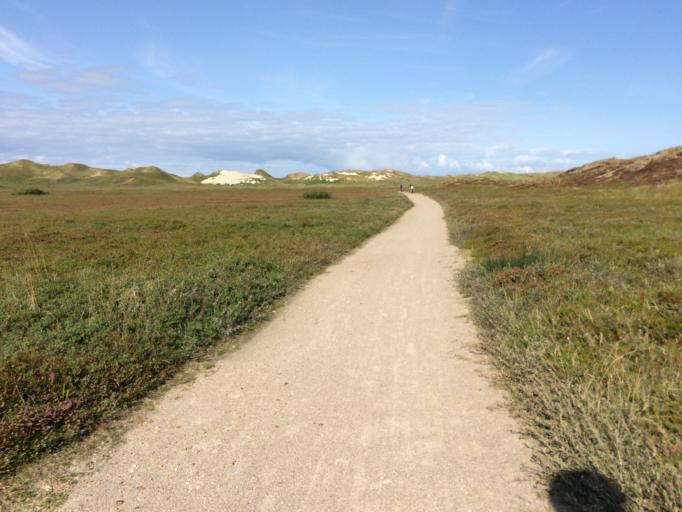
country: DK
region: Central Jutland
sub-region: Ringkobing-Skjern Kommune
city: Hvide Sande
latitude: 55.9174
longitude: 8.1605
